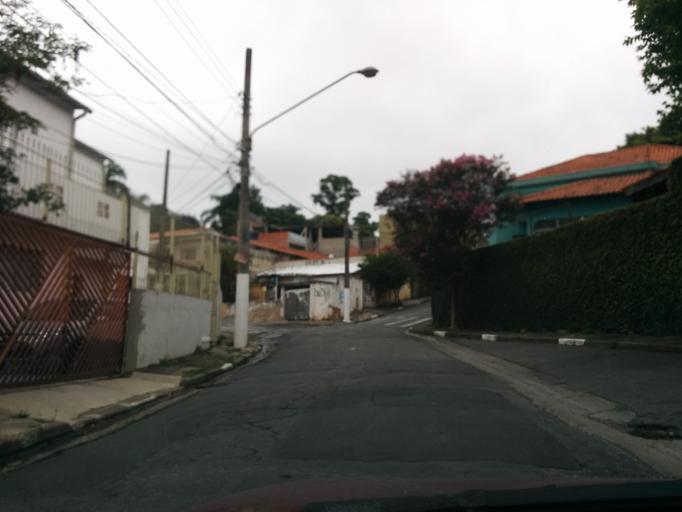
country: BR
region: Sao Paulo
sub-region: Osasco
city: Osasco
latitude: -23.5291
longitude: -46.8006
